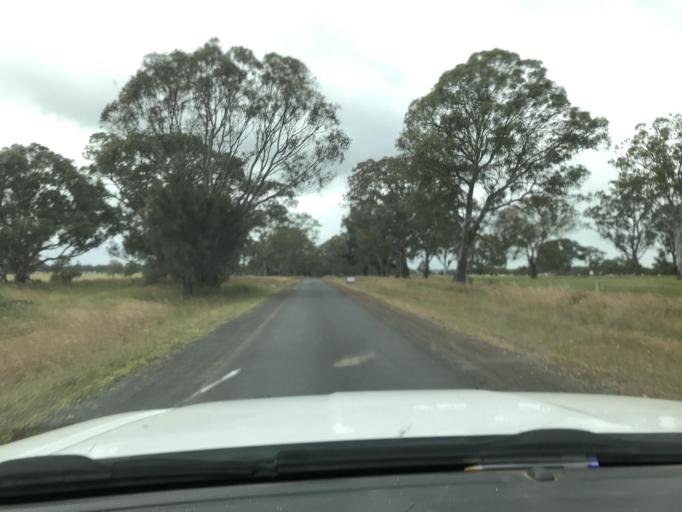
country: AU
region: South Australia
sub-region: Wattle Range
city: Penola
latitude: -37.1903
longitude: 141.4501
